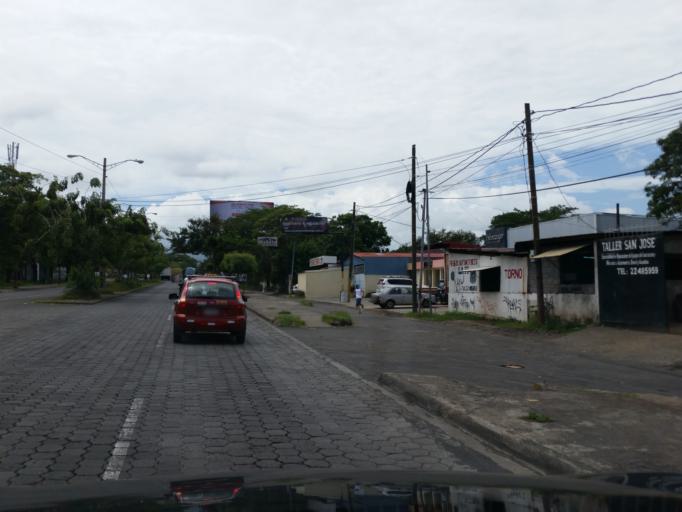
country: NI
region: Managua
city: Managua
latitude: 12.1328
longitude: -86.2303
